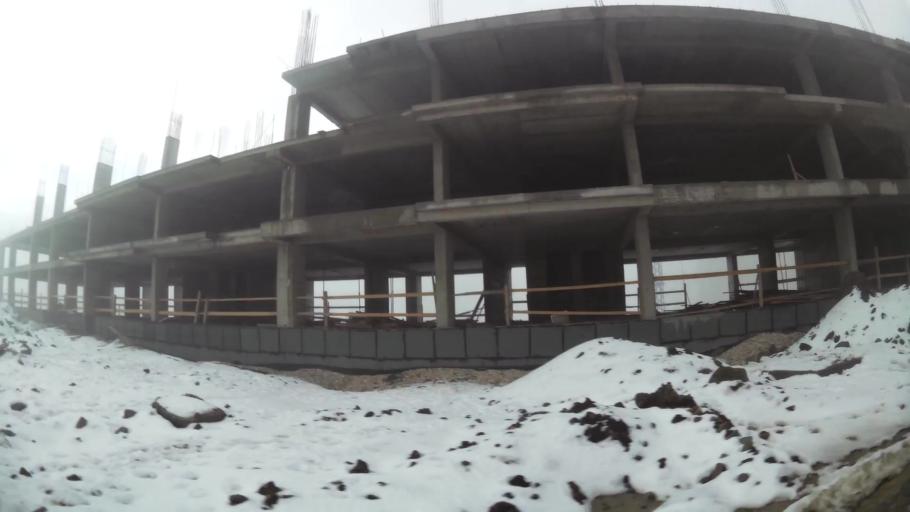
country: XK
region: Pristina
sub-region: Komuna e Prishtines
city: Pristina
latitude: 42.6405
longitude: 21.1514
